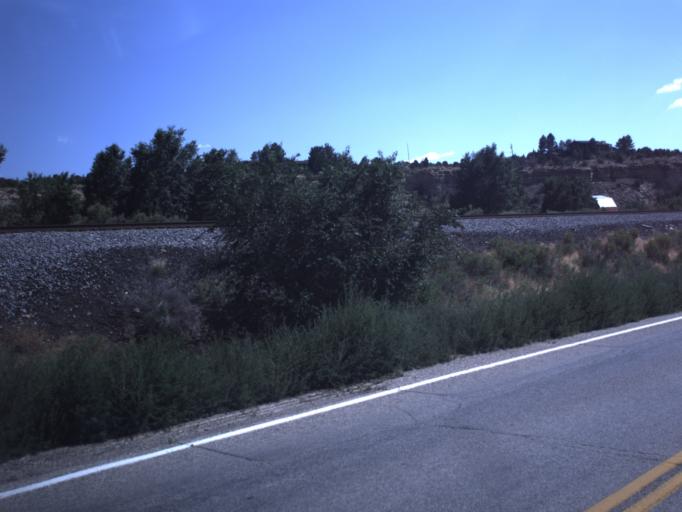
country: US
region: Utah
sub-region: Carbon County
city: Spring Glen
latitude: 39.6507
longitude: -110.8561
